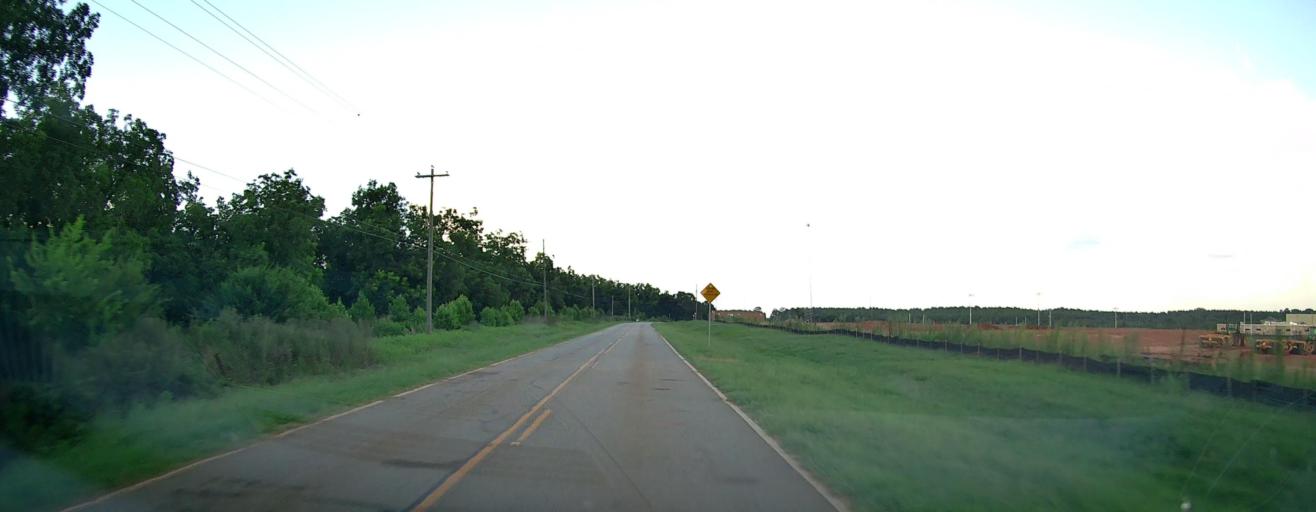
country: US
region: Georgia
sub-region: Peach County
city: Fort Valley
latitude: 32.5913
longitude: -83.8440
